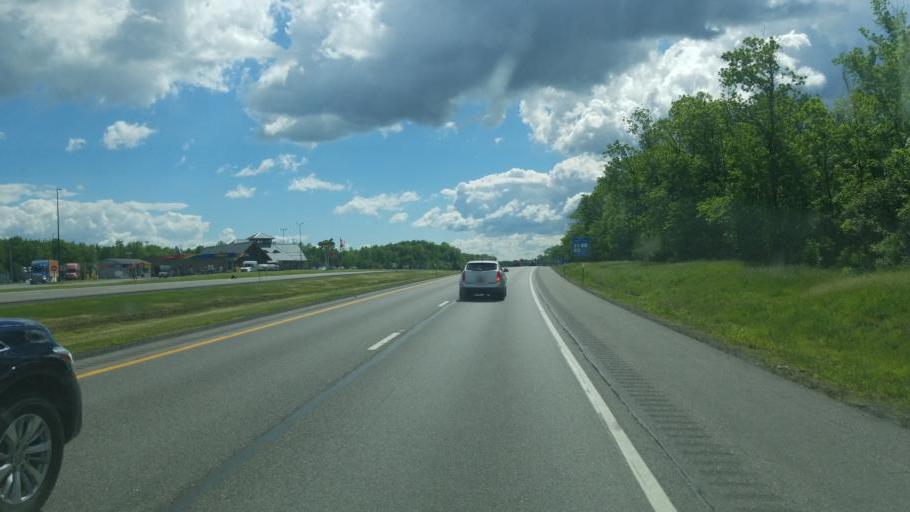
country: US
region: New York
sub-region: Madison County
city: Bolivar
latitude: 43.0955
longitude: -75.8447
